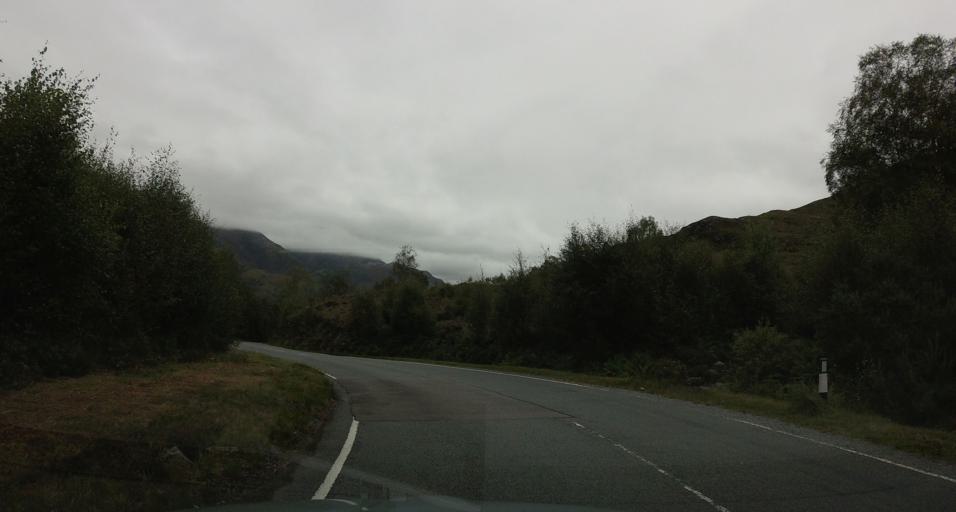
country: GB
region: Scotland
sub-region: Highland
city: Fort William
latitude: 56.7016
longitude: -5.0353
